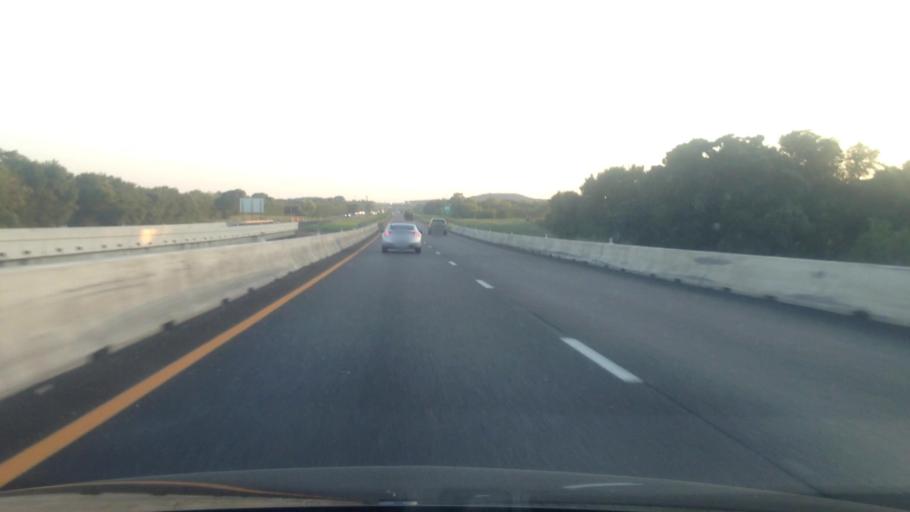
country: US
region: Texas
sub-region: Denton County
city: Denton
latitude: 33.1861
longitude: -97.1726
